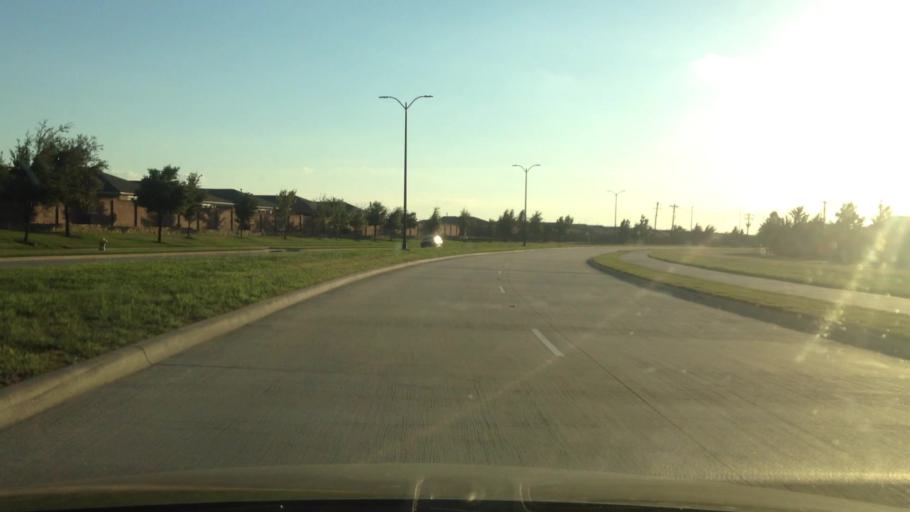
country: US
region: Texas
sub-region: Denton County
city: Little Elm
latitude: 33.1416
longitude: -96.9115
